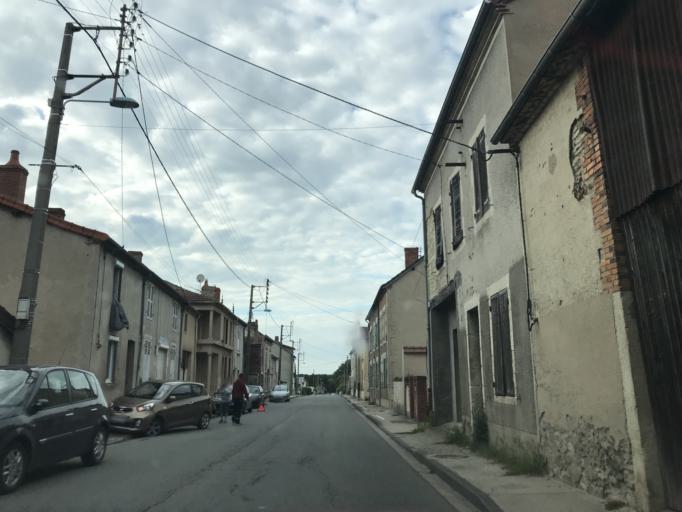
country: FR
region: Auvergne
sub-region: Departement du Puy-de-Dome
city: Randan
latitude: 46.0192
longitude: 3.3551
